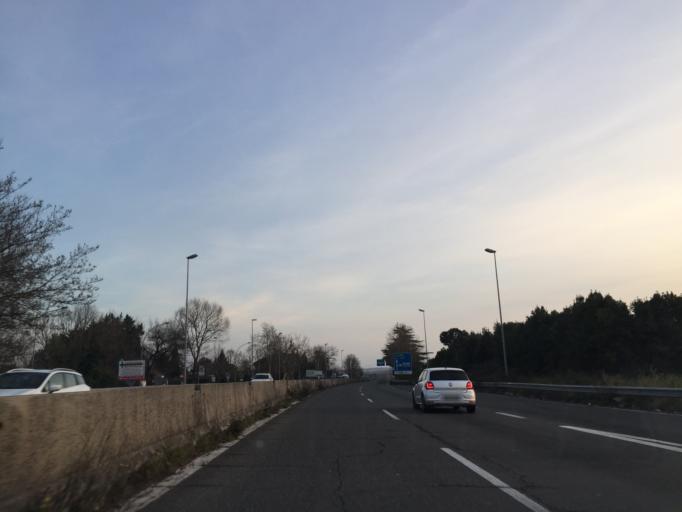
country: IT
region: Latium
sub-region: Citta metropolitana di Roma Capitale
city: Le Rughe
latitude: 42.0617
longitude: 12.3729
